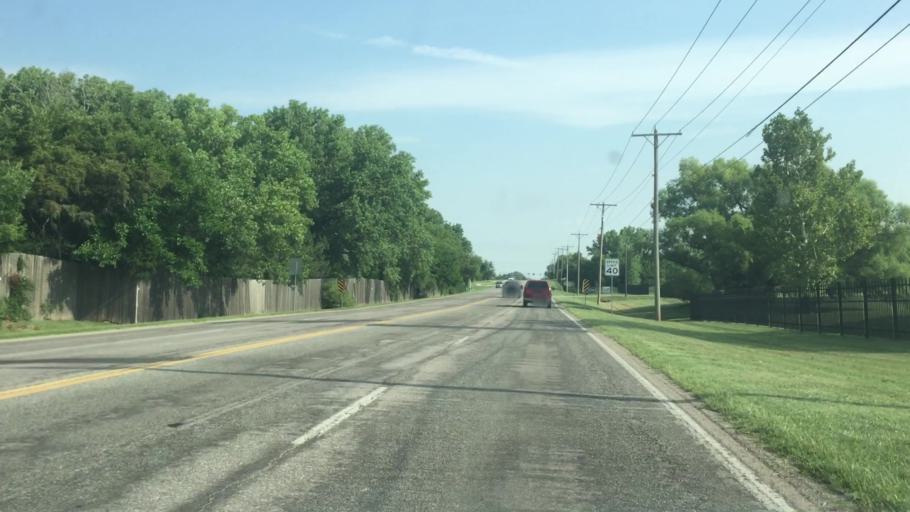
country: US
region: Kansas
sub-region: Sedgwick County
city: Bellaire
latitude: 37.7024
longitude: -97.2262
